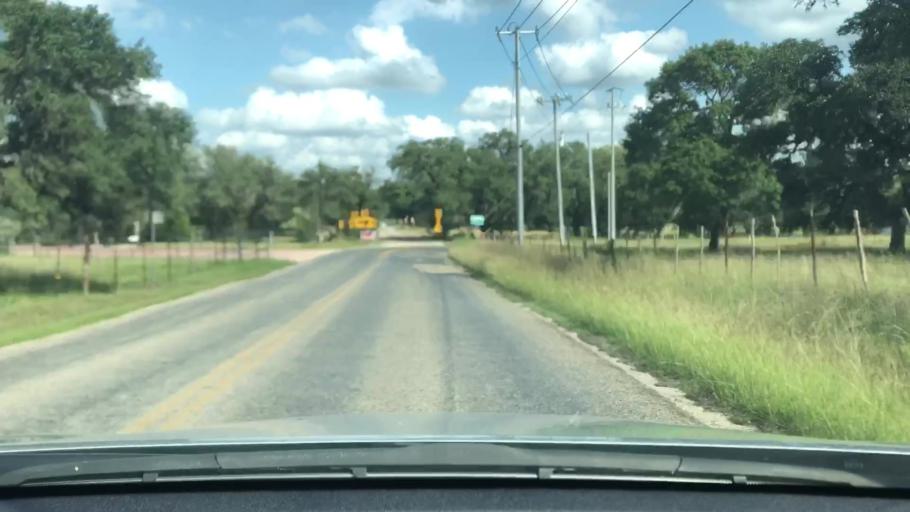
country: US
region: Texas
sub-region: Bexar County
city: Fair Oaks Ranch
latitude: 29.7851
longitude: -98.6275
